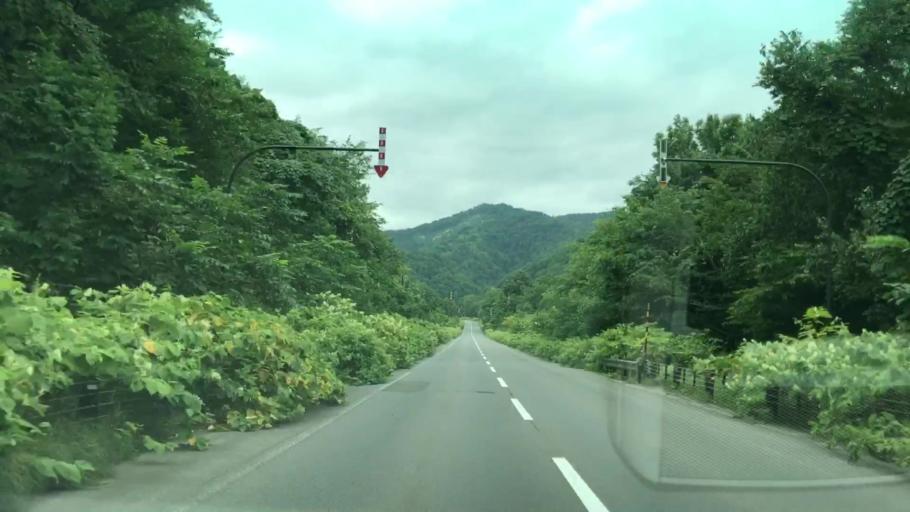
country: JP
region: Hokkaido
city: Yoichi
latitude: 43.0194
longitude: 140.8678
